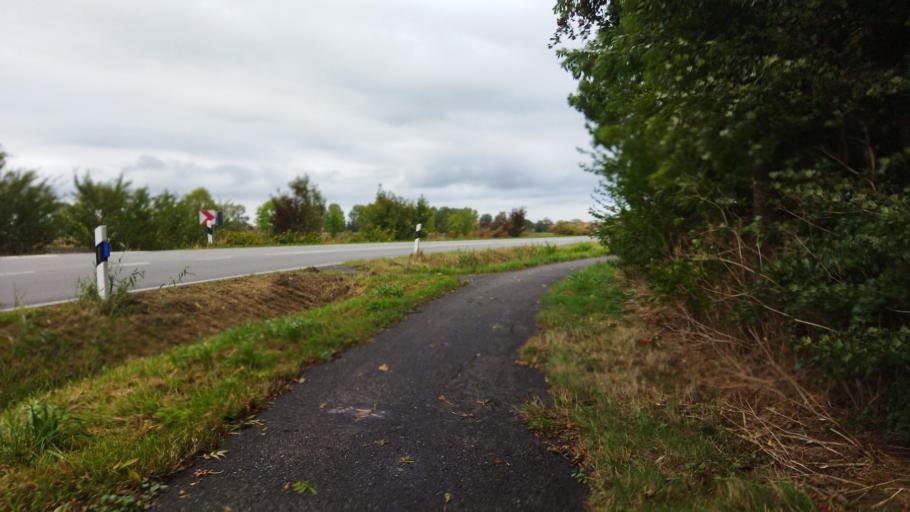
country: DE
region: Lower Saxony
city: Wirdum
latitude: 53.4798
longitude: 7.1375
